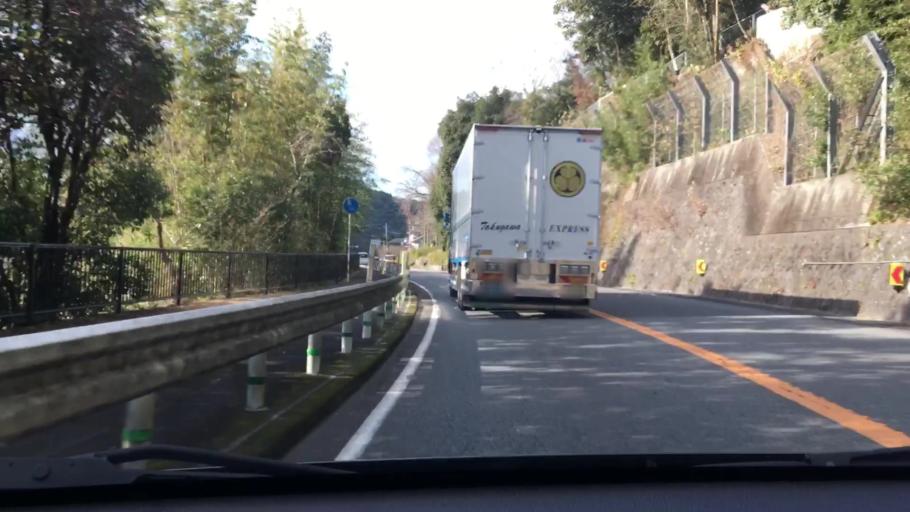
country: JP
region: Oita
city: Usuki
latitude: 33.0100
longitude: 131.7068
